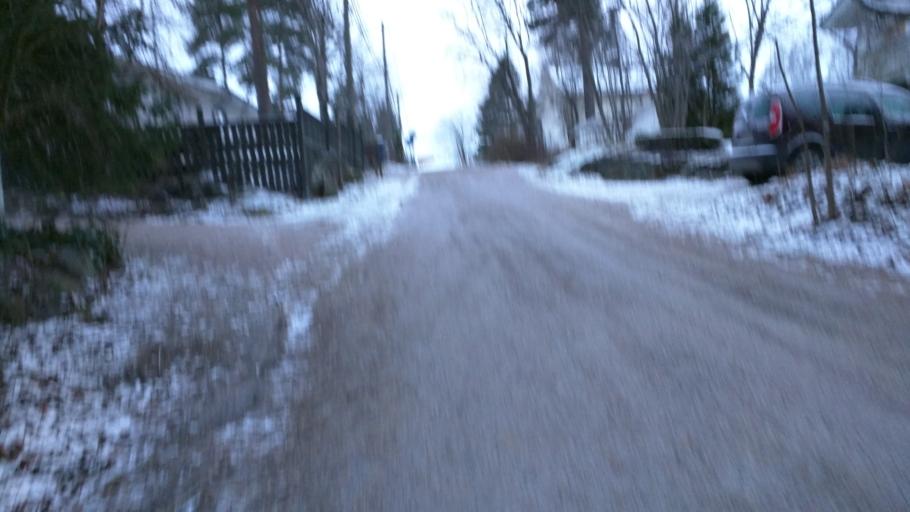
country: FI
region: Uusimaa
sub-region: Helsinki
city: Kilo
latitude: 60.2488
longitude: 24.7738
